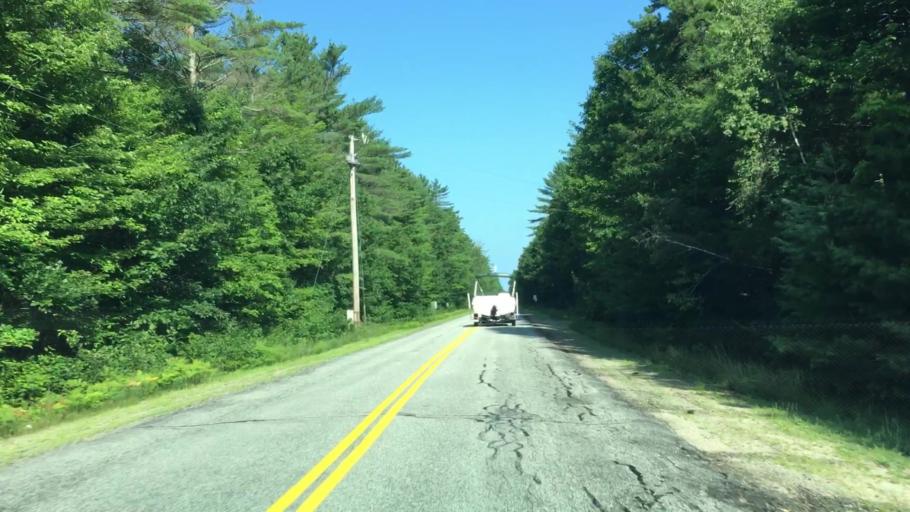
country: US
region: Maine
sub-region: Androscoggin County
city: Poland
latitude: 44.0441
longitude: -70.3565
